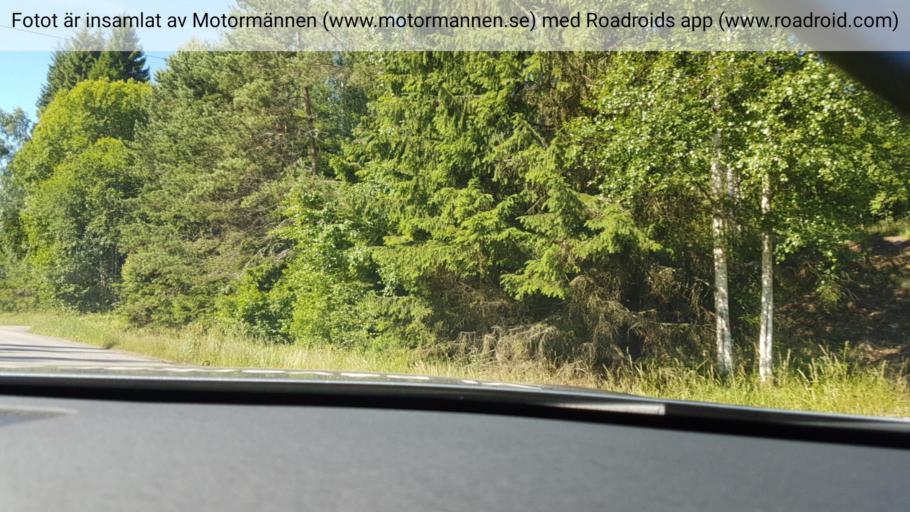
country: SE
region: Vaestra Goetaland
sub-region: Ulricehamns Kommun
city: Ulricehamn
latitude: 57.8284
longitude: 13.2906
